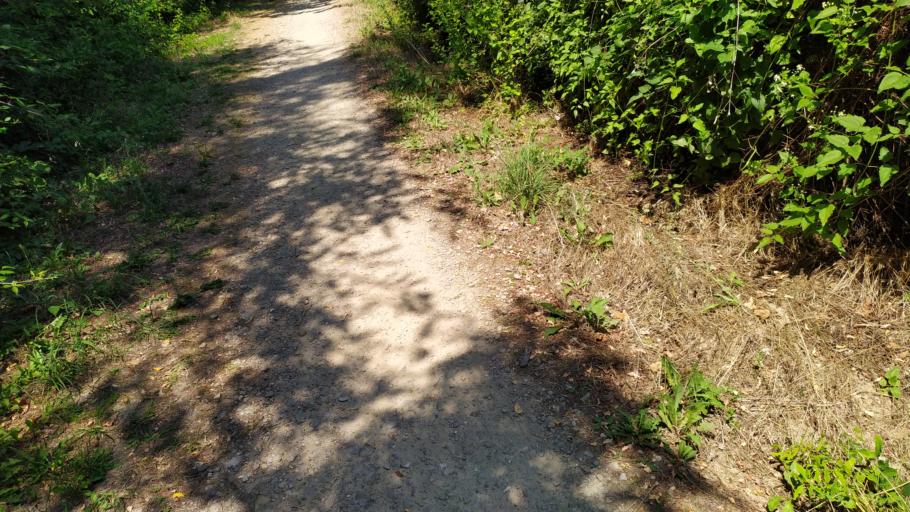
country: IT
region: Emilia-Romagna
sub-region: Forli-Cesena
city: Castrocaro Terme e Terra del Sole
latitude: 44.2011
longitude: 11.9918
